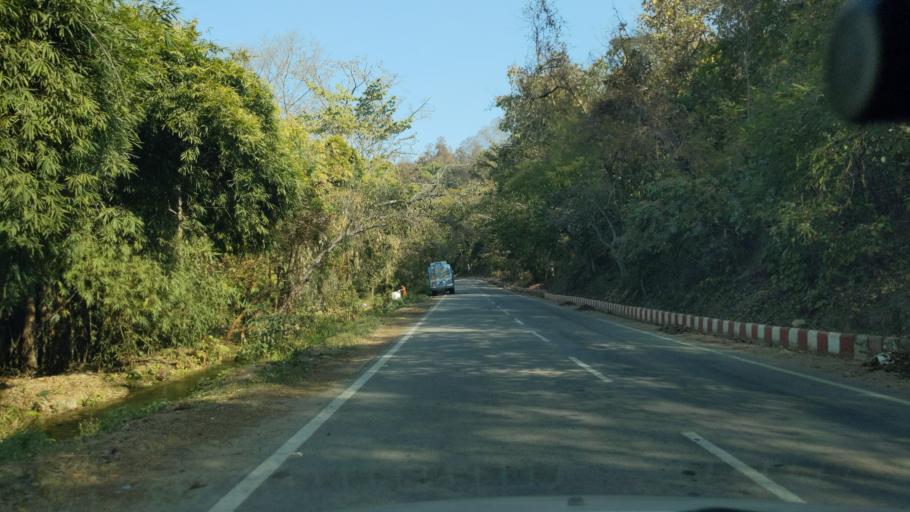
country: IN
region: Uttarakhand
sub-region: Naini Tal
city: Ramnagar
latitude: 29.3917
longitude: 79.1378
